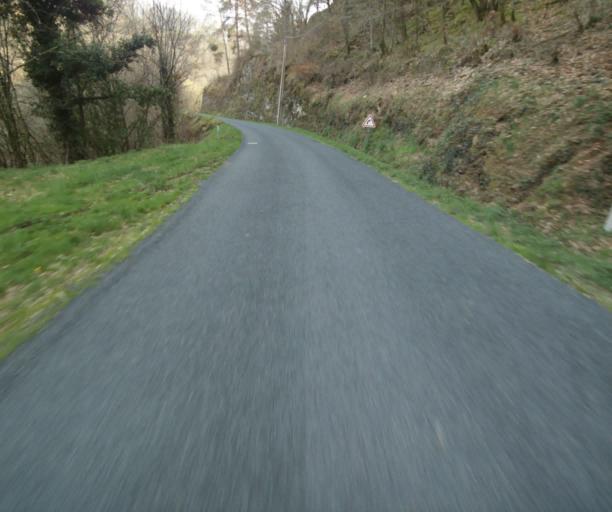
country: FR
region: Limousin
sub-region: Departement de la Correze
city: Naves
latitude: 45.3358
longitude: 1.7910
